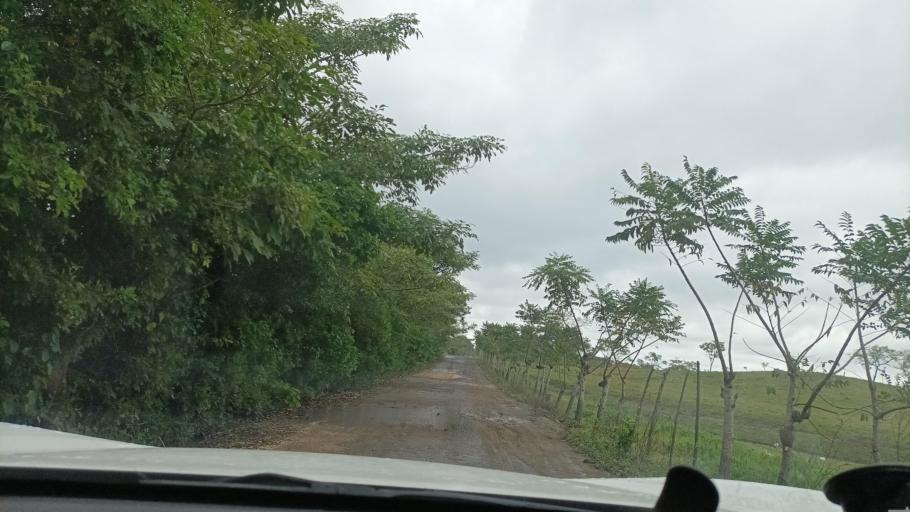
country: MX
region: Veracruz
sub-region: Moloacan
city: Cuichapa
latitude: 17.7678
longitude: -94.3886
